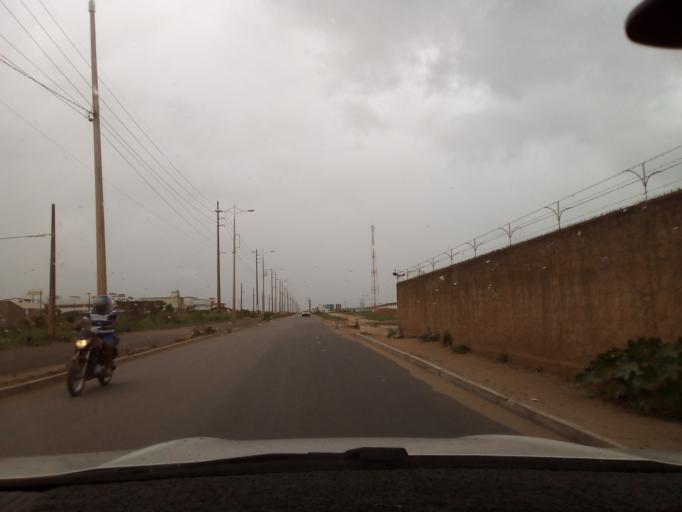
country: BR
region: Paraiba
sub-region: Conde
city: Conde
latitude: -7.1998
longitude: -34.8760
